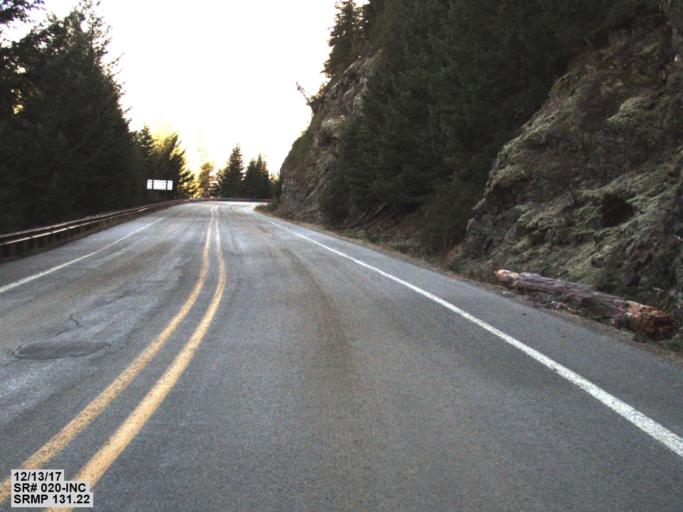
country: US
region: Washington
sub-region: Snohomish County
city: Darrington
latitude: 48.7029
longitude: -121.0958
